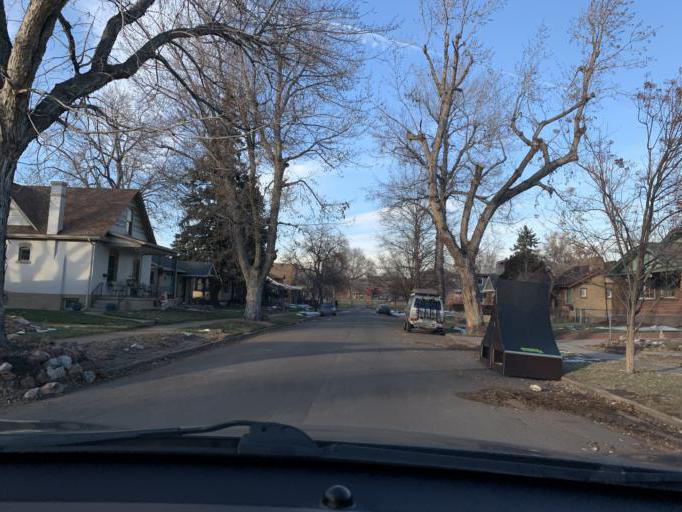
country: US
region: Colorado
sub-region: Adams County
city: Berkley
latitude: 39.7720
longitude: -105.0358
